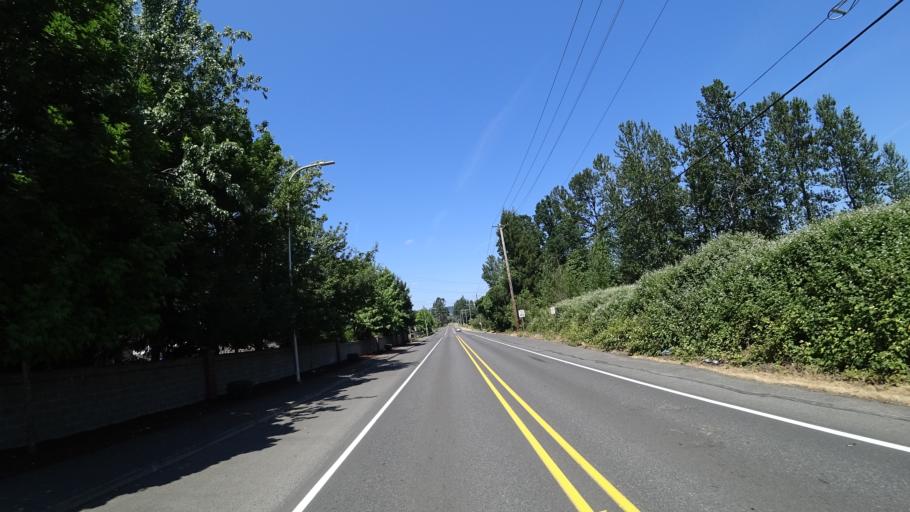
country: US
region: Oregon
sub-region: Multnomah County
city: Fairview
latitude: 45.5480
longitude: -122.4334
